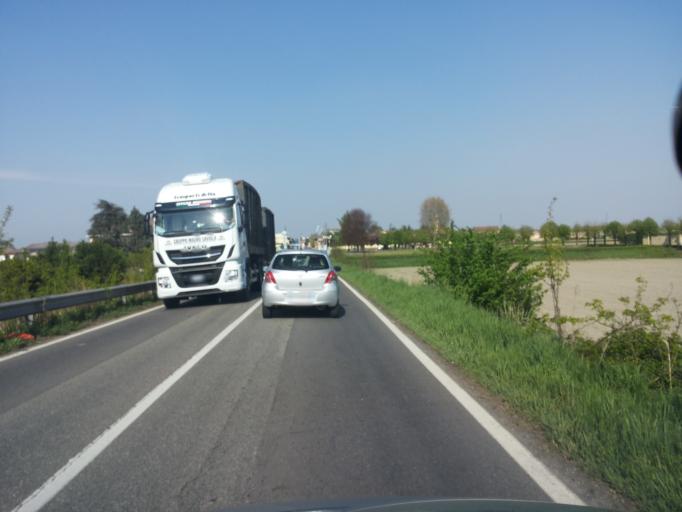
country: IT
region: Lombardy
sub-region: Provincia di Pavia
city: Castello d'Agogna
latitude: 45.2310
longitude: 8.6837
